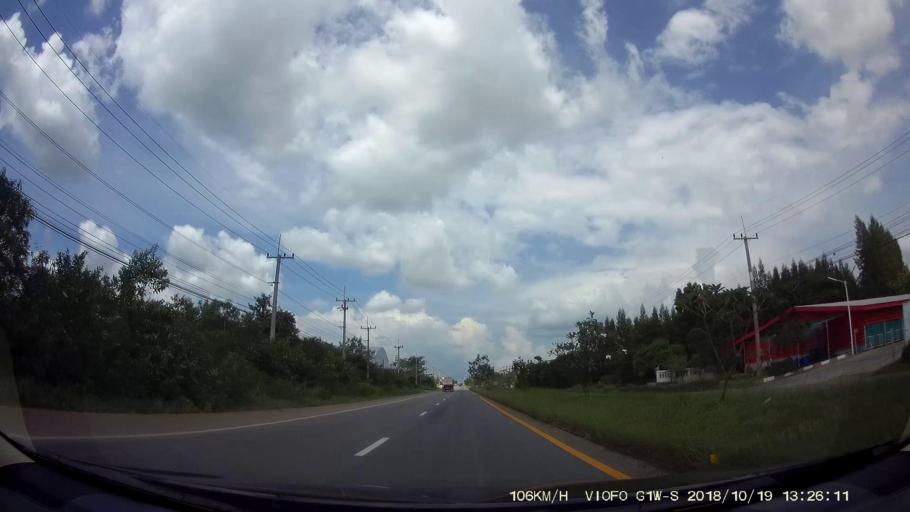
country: TH
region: Chaiyaphum
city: Chatturat
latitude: 15.5315
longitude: 101.8316
